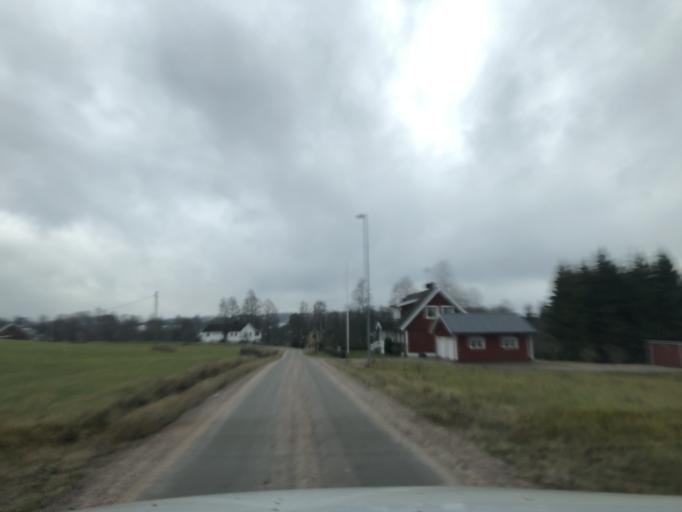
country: SE
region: Vaestra Goetaland
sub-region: Ulricehamns Kommun
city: Ulricehamn
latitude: 57.8663
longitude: 13.5547
